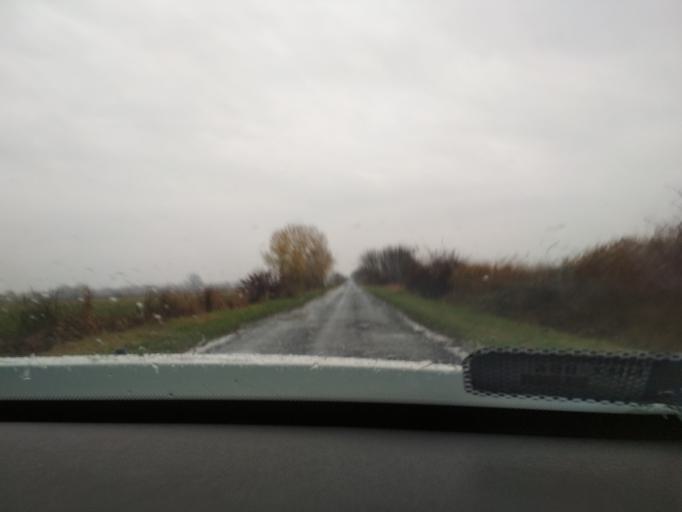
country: HU
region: Csongrad
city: Baks
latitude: 46.5397
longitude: 20.1125
